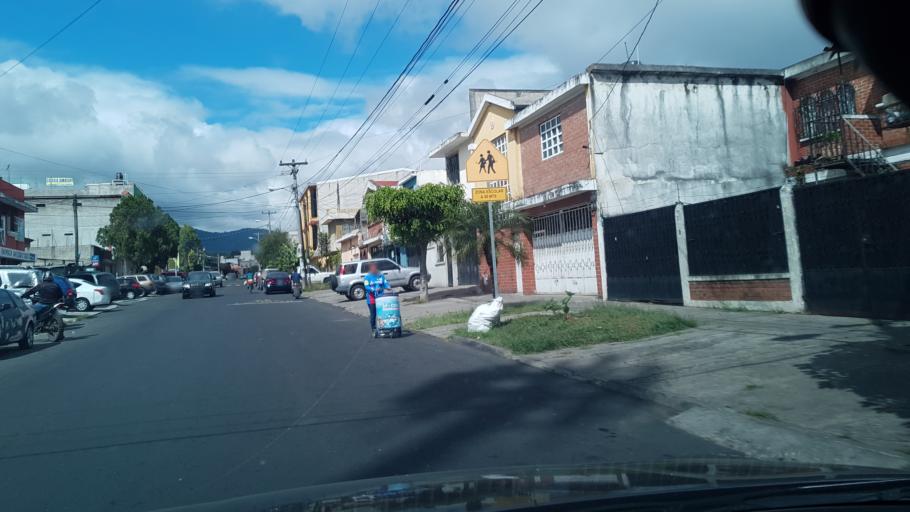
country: GT
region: Guatemala
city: Mixco
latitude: 14.6415
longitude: -90.5767
